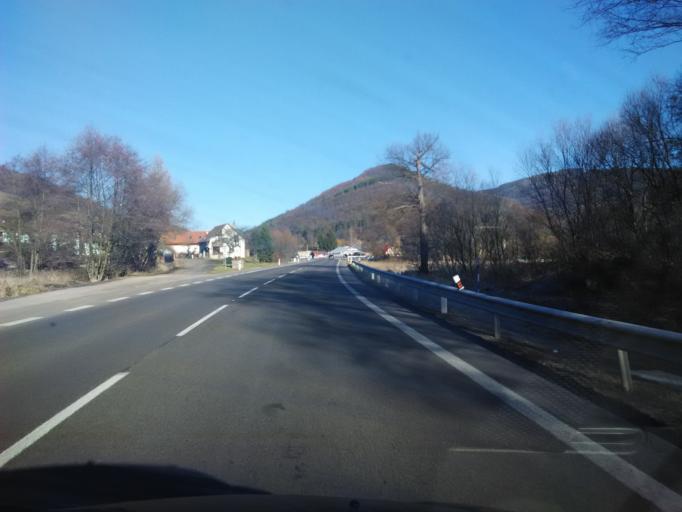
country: SK
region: Banskobystricky
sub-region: Okres Ziar nad Hronom
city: Kremnica
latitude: 48.6611
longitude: 18.9108
